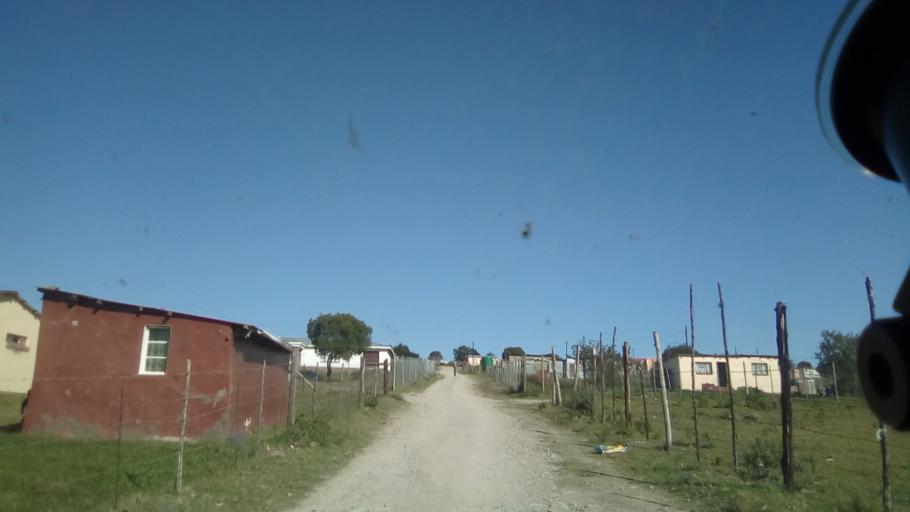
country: ZA
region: Eastern Cape
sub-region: Buffalo City Metropolitan Municipality
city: Bhisho
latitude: -32.8336
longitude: 27.3677
